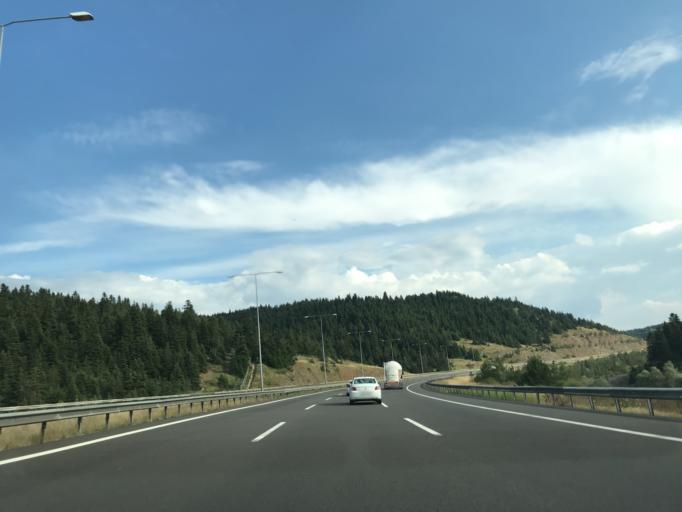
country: TR
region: Ankara
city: Pecenek
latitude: 40.5972
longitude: 32.2863
